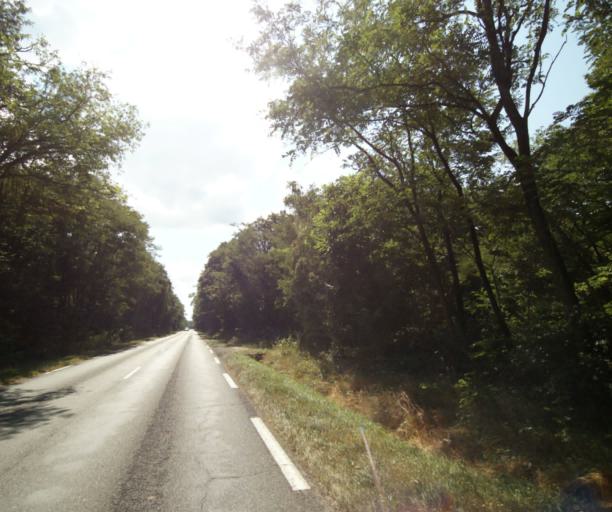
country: FR
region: Centre
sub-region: Departement du Loiret
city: Saint-Cyr-en-Val
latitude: 47.8219
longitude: 1.9834
